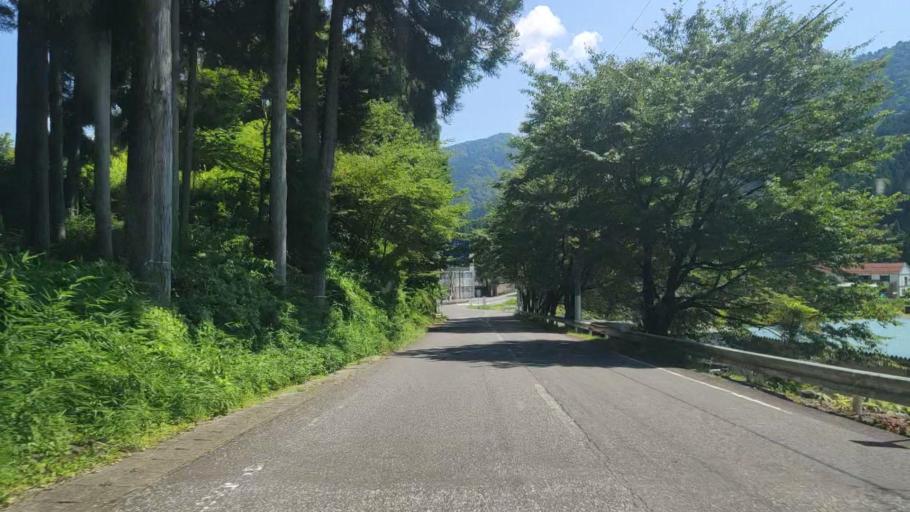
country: JP
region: Gifu
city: Godo
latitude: 35.6266
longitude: 136.6196
